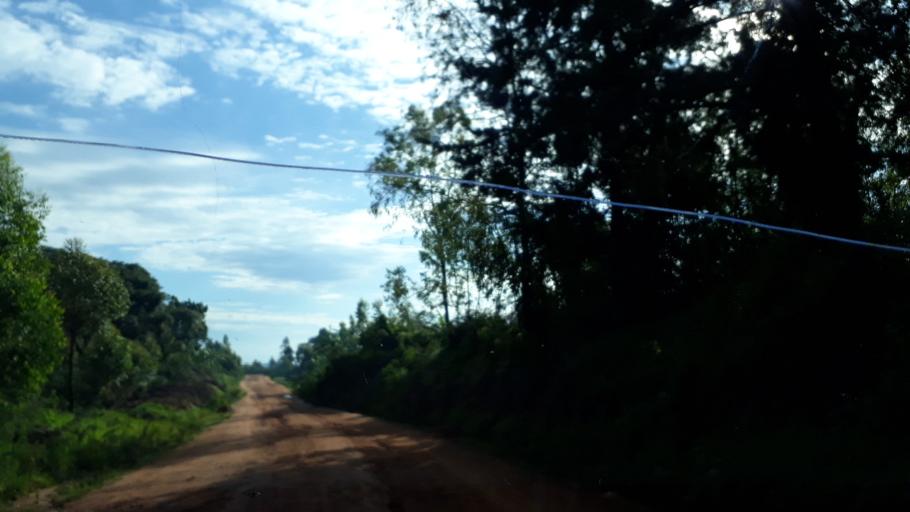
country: UG
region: Northern Region
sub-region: Zombo District
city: Paidha
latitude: 2.2511
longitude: 30.9260
